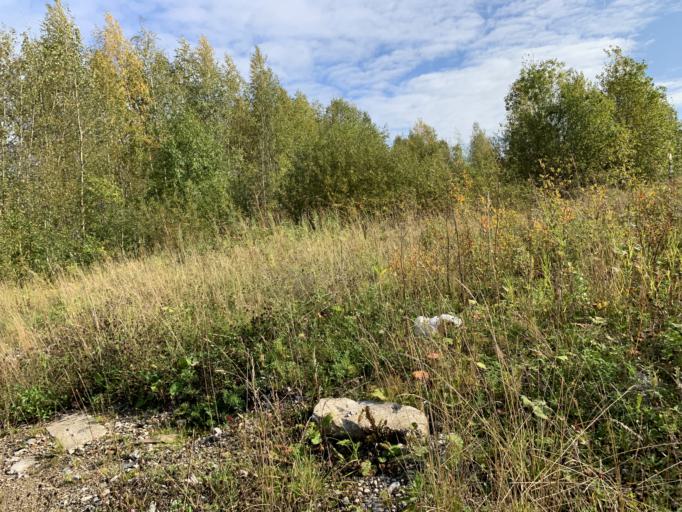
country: RU
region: Perm
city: Gubakha
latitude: 58.8354
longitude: 57.5594
